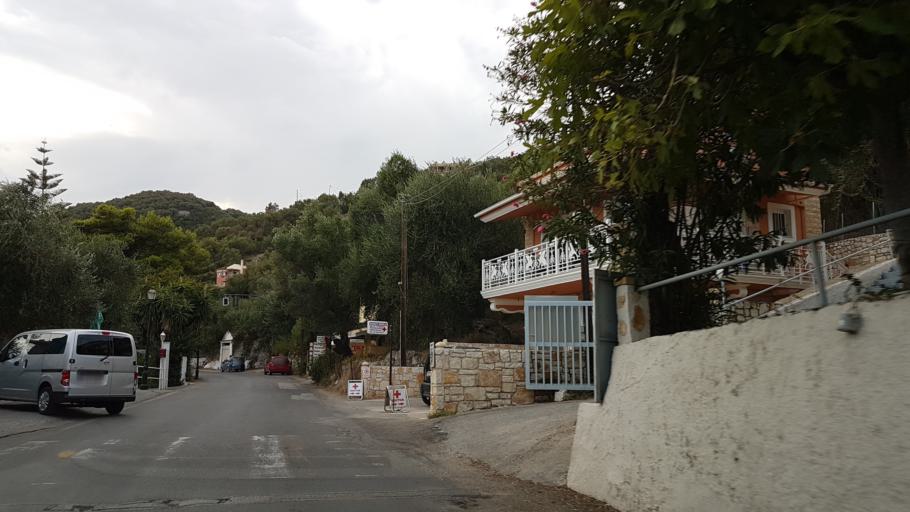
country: GR
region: Ionian Islands
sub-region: Nomos Kerkyras
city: Kontokali
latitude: 39.7192
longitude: 19.8688
